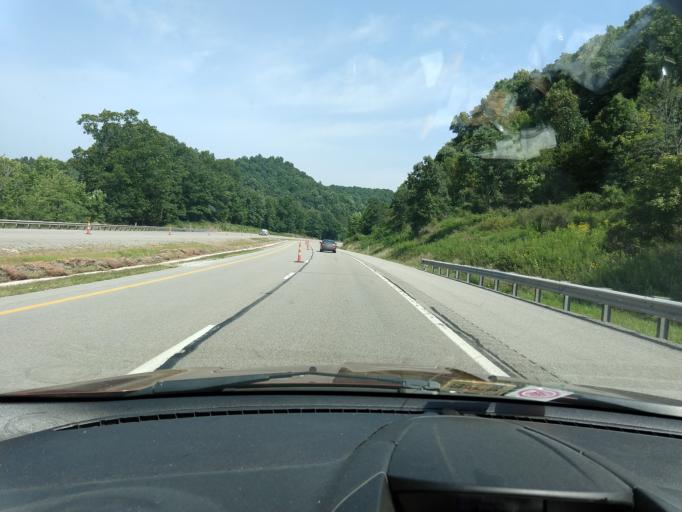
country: US
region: West Virginia
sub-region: Lewis County
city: Weston
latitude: 38.9935
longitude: -80.5046
